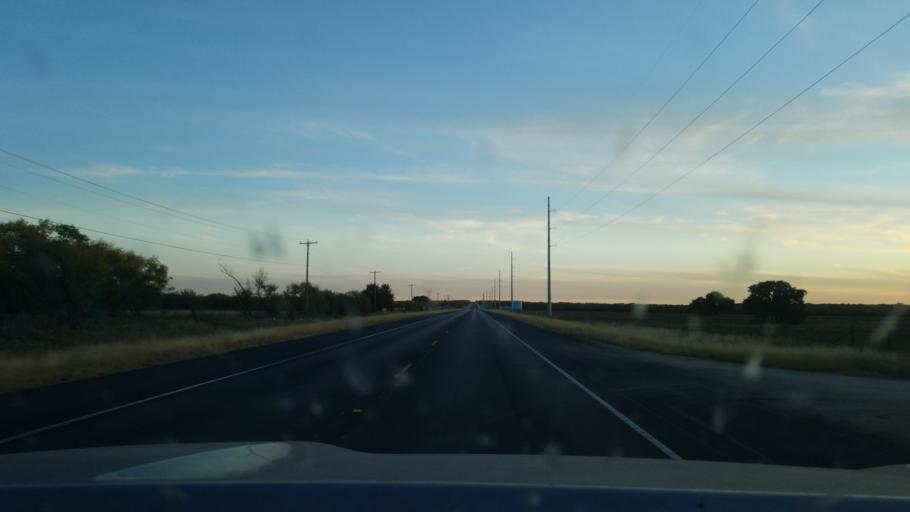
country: US
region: Texas
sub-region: Stephens County
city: Breckenridge
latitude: 32.7140
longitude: -98.9027
